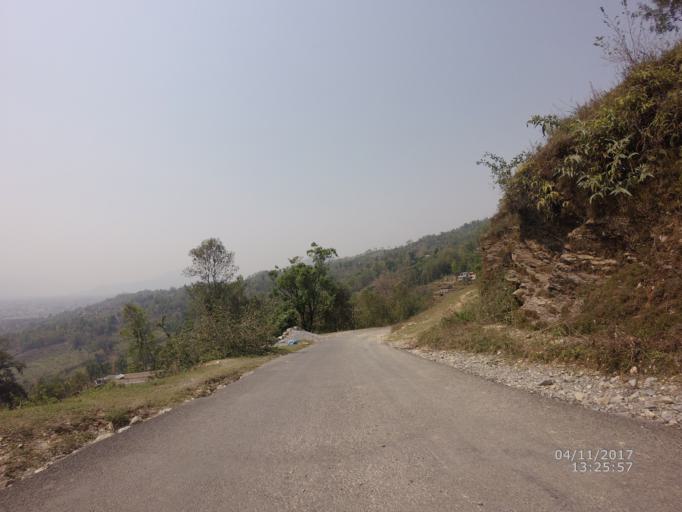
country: NP
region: Western Region
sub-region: Gandaki Zone
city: Pokhara
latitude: 28.2016
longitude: 84.0427
